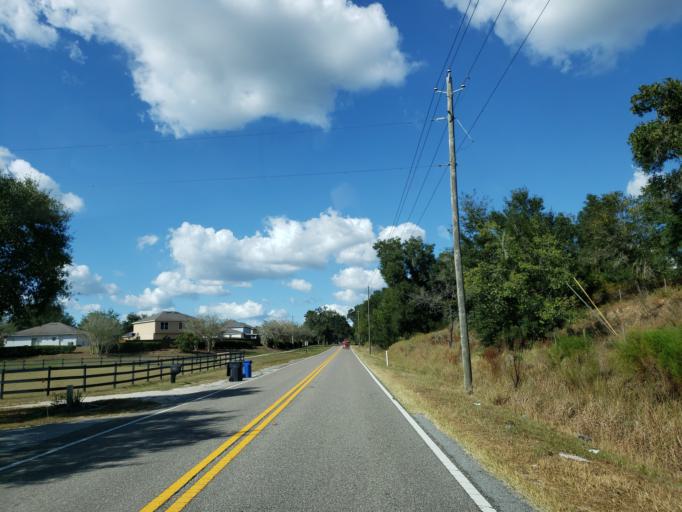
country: US
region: Florida
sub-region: Hillsborough County
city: Valrico
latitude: 27.9179
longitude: -82.2195
